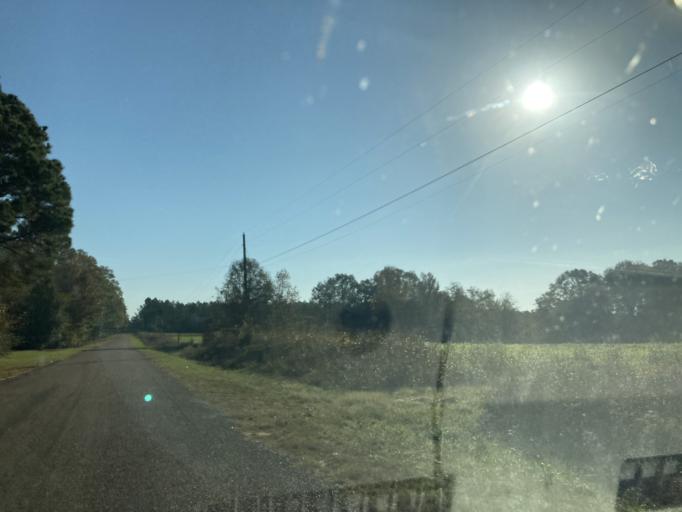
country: US
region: Mississippi
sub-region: Madison County
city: Canton
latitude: 32.7130
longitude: -90.1753
